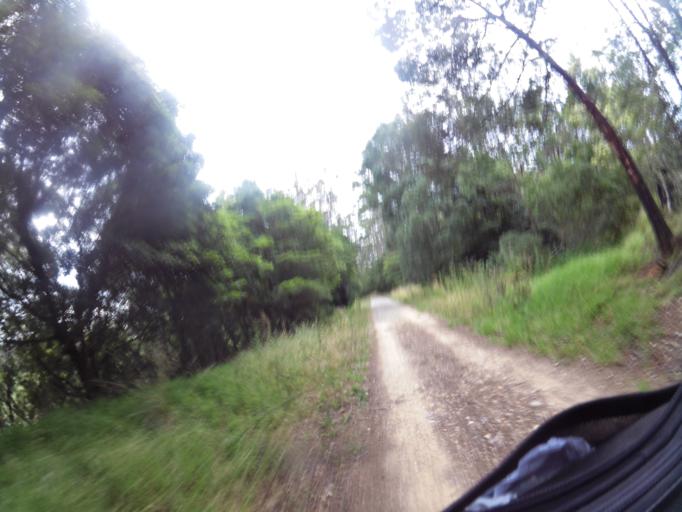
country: AU
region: Victoria
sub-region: East Gippsland
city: Lakes Entrance
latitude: -37.7264
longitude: 148.4270
